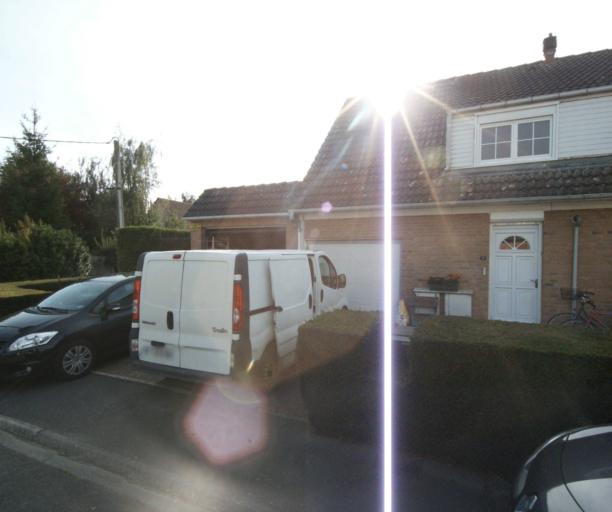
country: FR
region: Nord-Pas-de-Calais
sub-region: Departement du Nord
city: Fournes-en-Weppes
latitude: 50.5849
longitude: 2.8831
